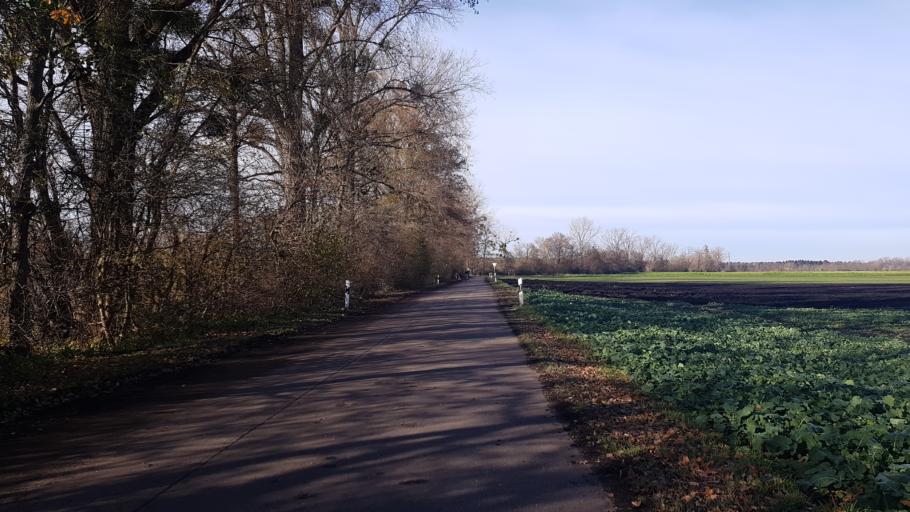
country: DE
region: Bavaria
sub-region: Upper Bavaria
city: Karlsfeld
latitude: 48.2290
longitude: 11.5085
